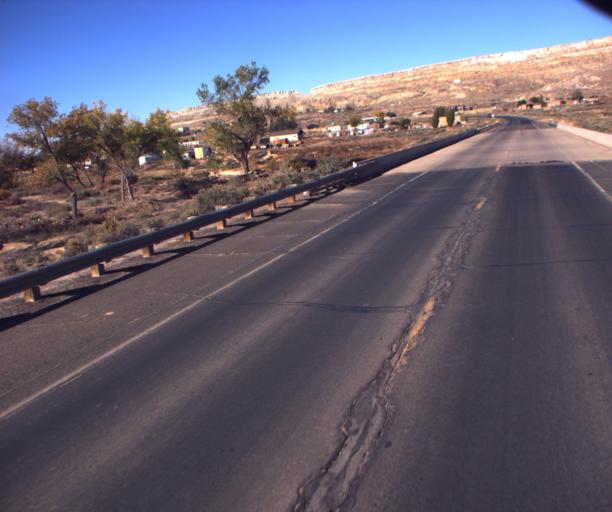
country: US
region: Arizona
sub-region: Navajo County
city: First Mesa
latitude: 35.8406
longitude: -110.3650
